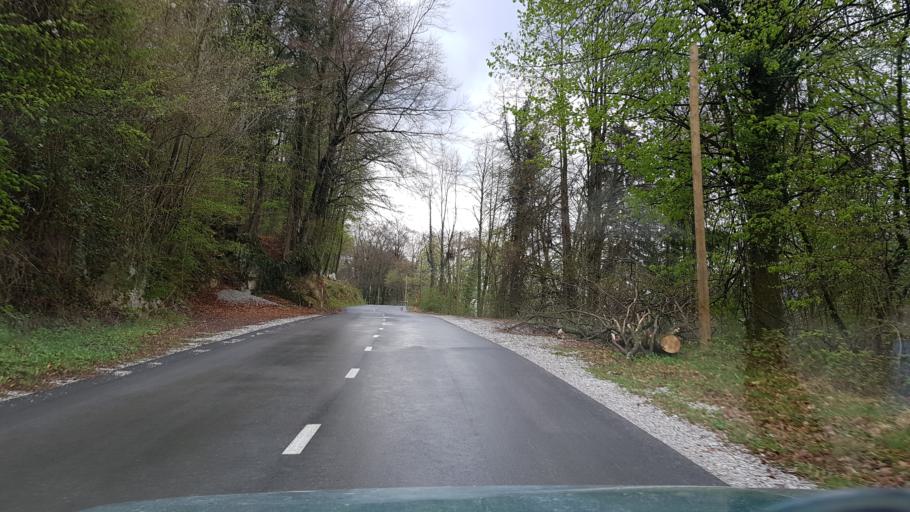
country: SI
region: Tolmin
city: Tolmin
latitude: 46.1158
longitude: 13.8192
